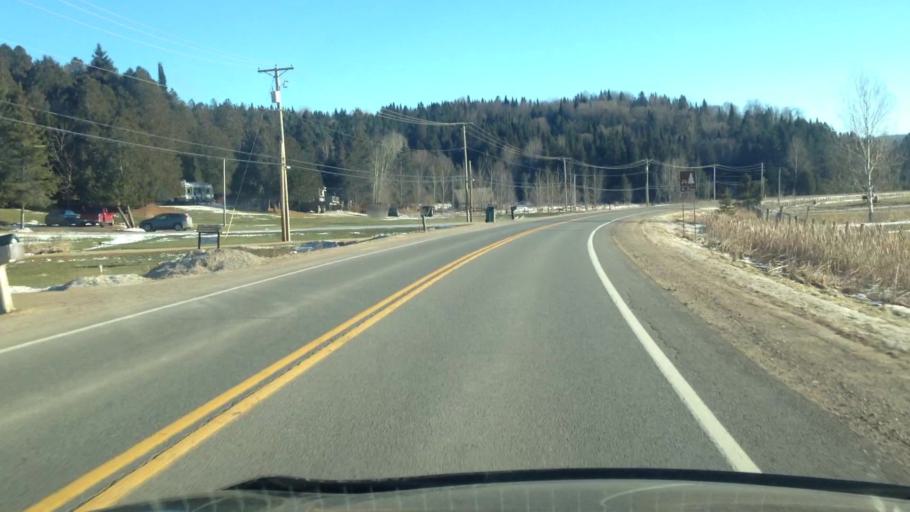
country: CA
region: Quebec
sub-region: Laurentides
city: Mont-Tremblant
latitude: 45.9582
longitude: -74.5686
